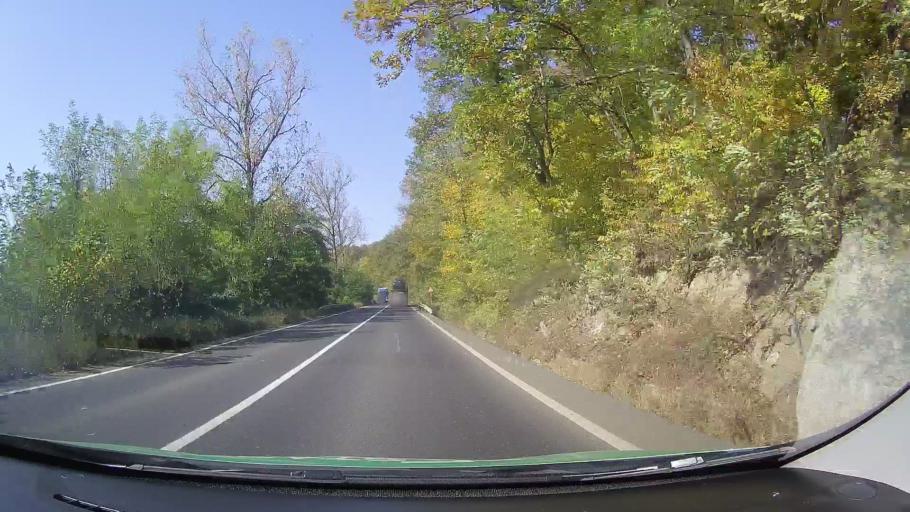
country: RO
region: Arad
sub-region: Comuna Varadia de Mures
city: Varadia de Mures
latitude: 46.0295
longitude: 22.1195
